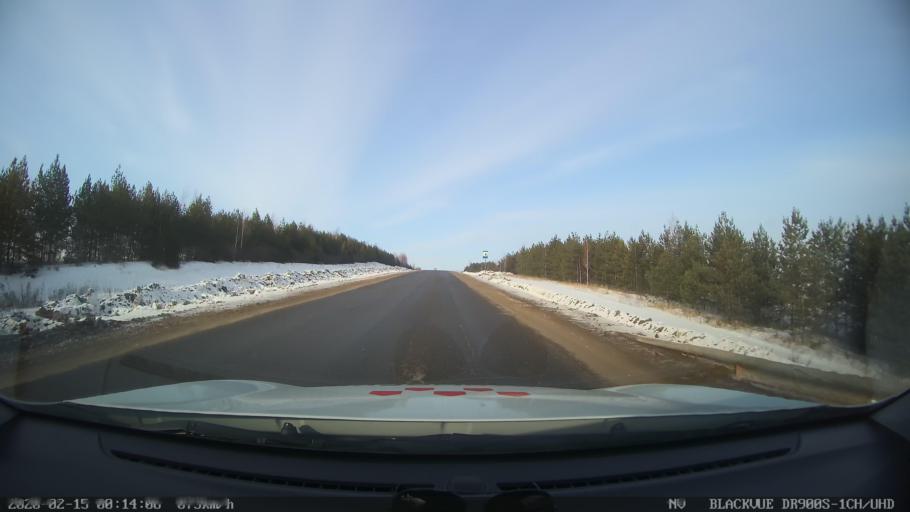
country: RU
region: Tatarstan
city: Stolbishchi
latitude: 55.4824
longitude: 49.0044
